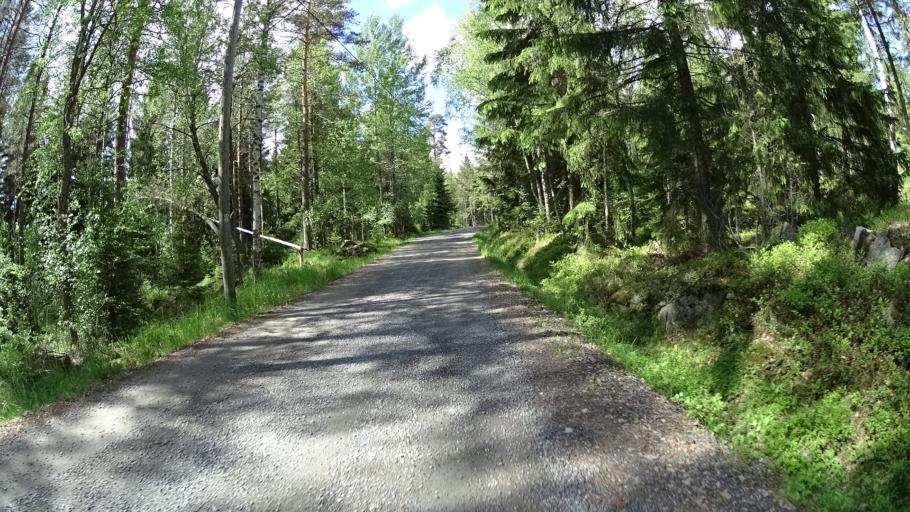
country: FI
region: Uusimaa
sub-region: Raaseporin
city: Pohja
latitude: 60.1817
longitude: 23.5850
